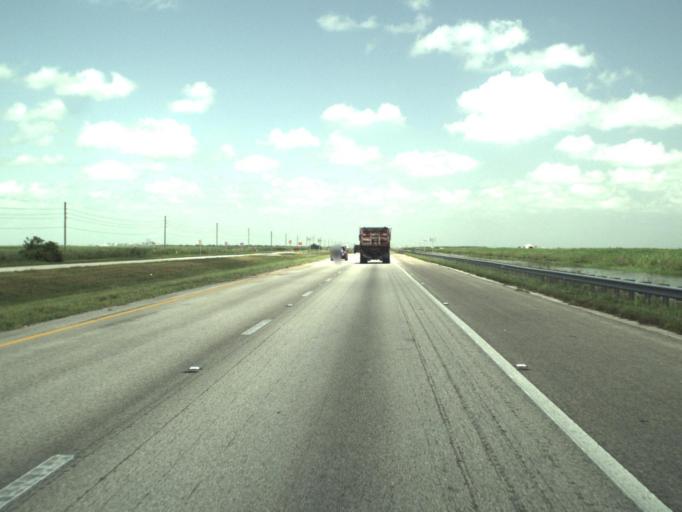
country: US
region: Florida
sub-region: Palm Beach County
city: Belle Glade Camp
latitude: 26.5304
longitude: -80.6891
